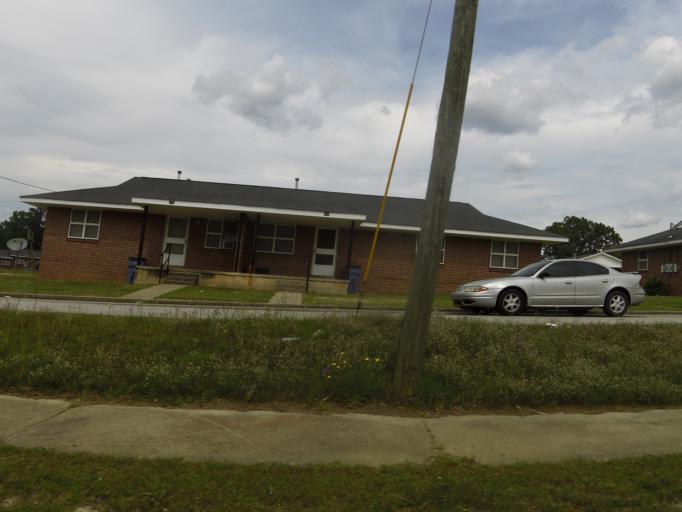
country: US
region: Georgia
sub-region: Jefferson County
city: Wrens
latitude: 33.2119
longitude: -82.3943
